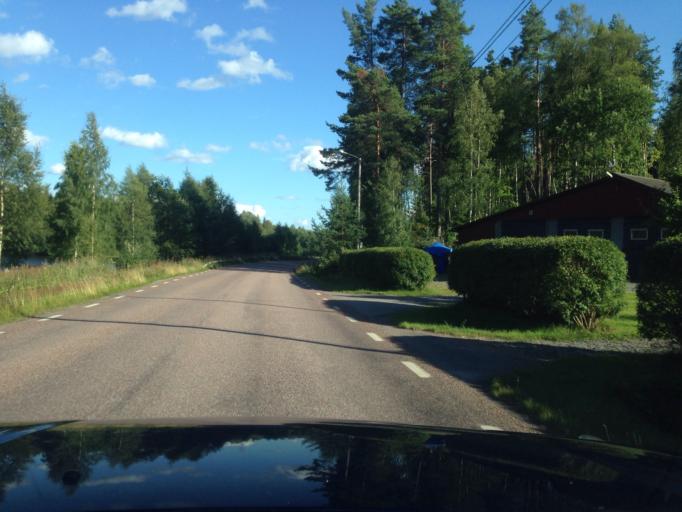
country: SE
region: Dalarna
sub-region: Ludvika Kommun
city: Grangesberg
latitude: 60.2082
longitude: 14.9609
